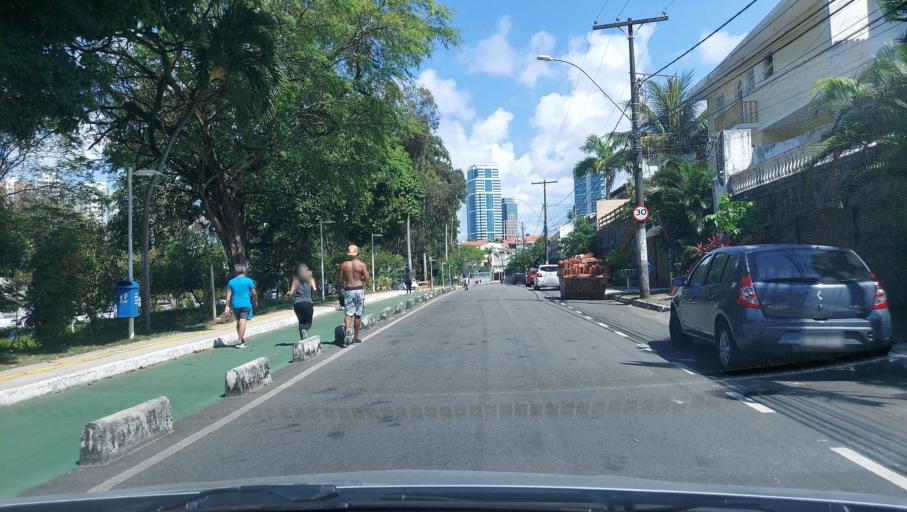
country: BR
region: Bahia
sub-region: Salvador
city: Salvador
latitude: -12.9842
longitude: -38.4560
